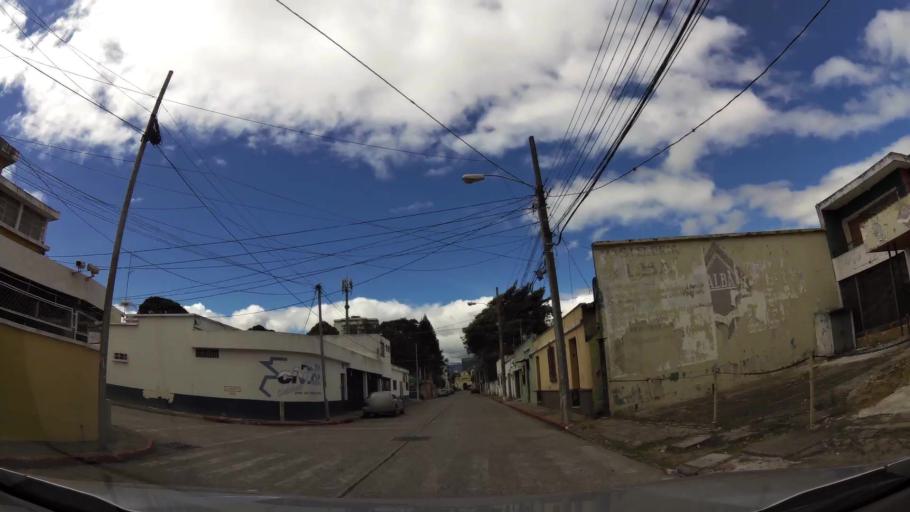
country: GT
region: Guatemala
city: Guatemala City
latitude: 14.6060
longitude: -90.5114
